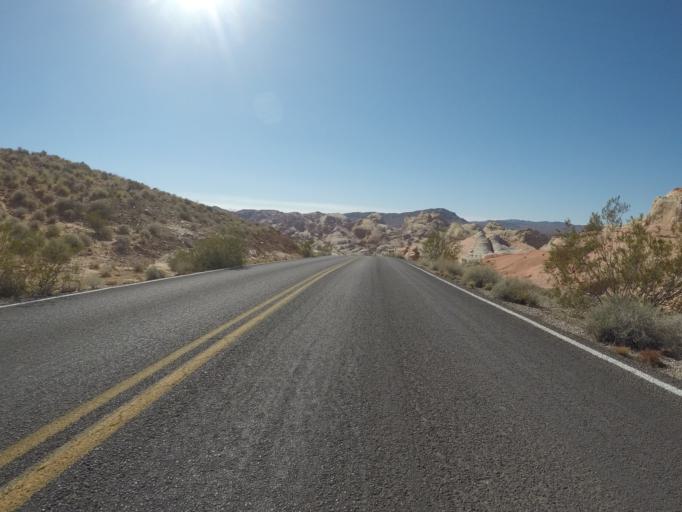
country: US
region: Nevada
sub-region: Clark County
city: Moapa Valley
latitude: 36.4862
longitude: -114.5266
